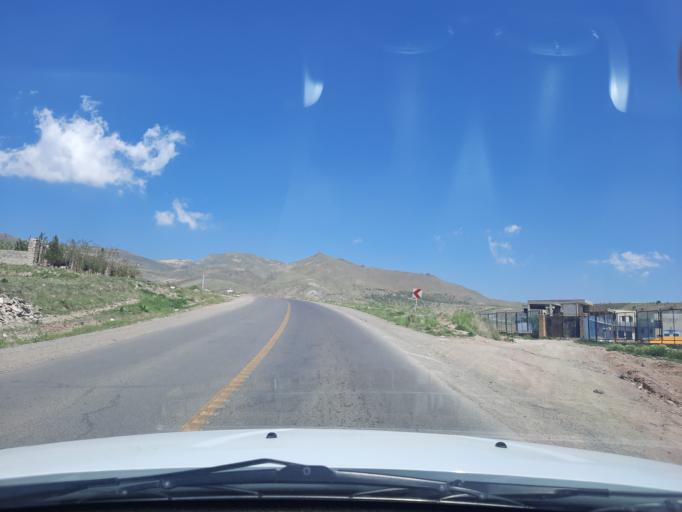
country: IR
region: Qazvin
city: Qazvin
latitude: 36.3465
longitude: 50.1830
